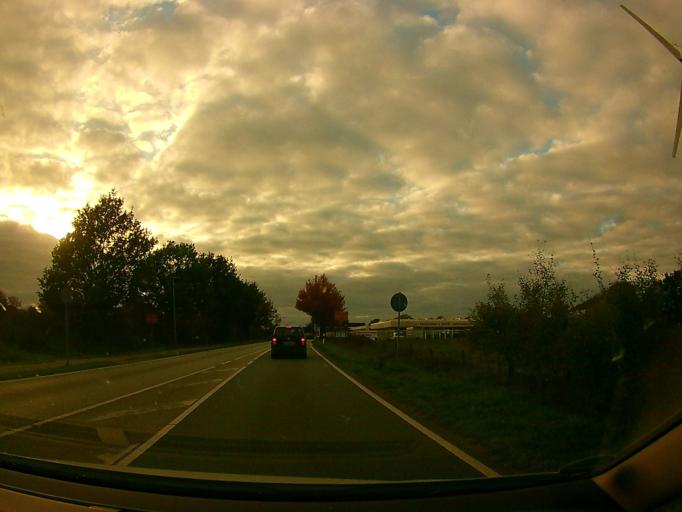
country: DE
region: Schleswig-Holstein
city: Silberstedt
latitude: 54.5177
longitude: 9.3874
